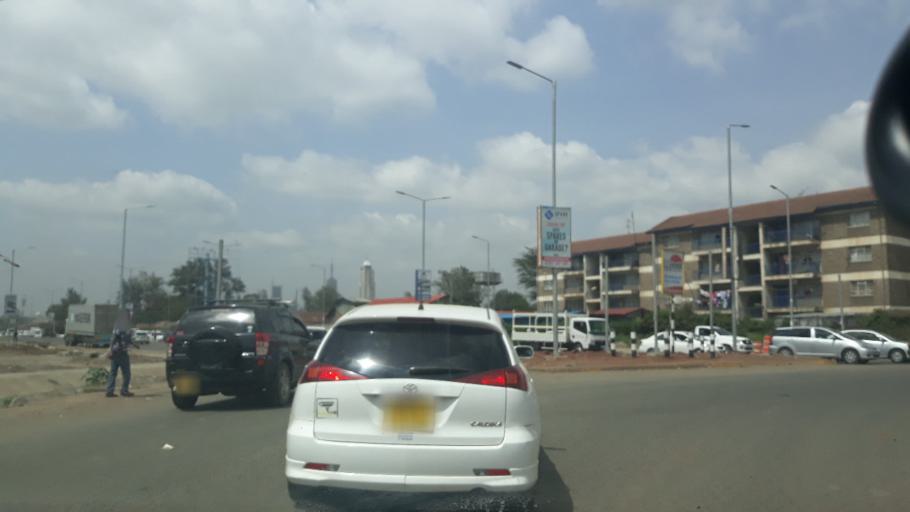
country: KE
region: Nairobi Area
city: Pumwani
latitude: -1.3000
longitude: 36.8368
